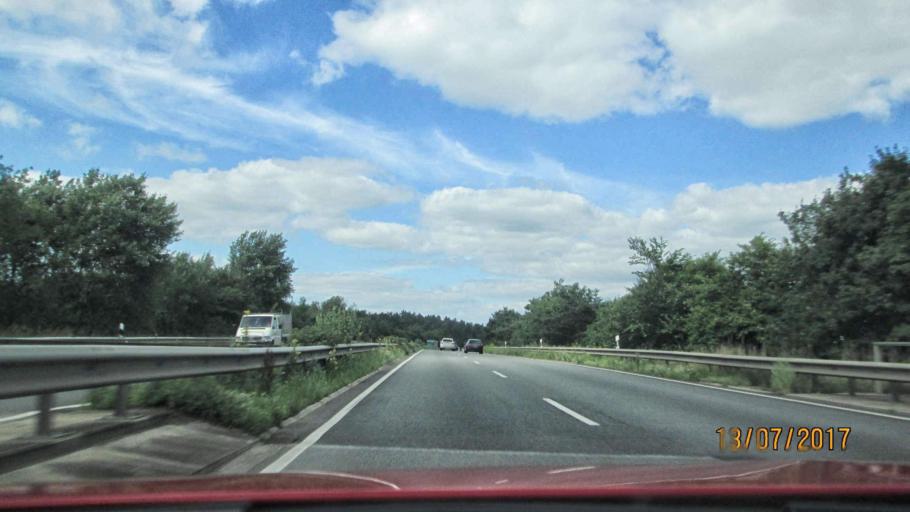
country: DE
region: Lower Saxony
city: Deutsch Evern
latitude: 53.2169
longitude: 10.4454
